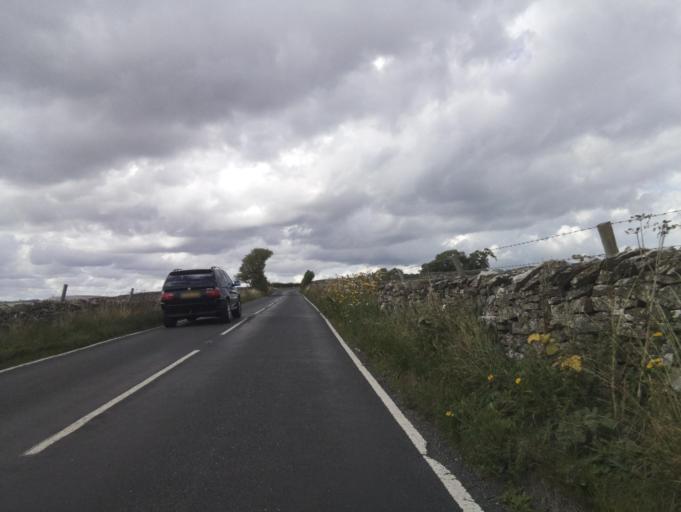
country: GB
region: England
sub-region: North Yorkshire
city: Leyburn
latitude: 54.3664
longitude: -1.8245
